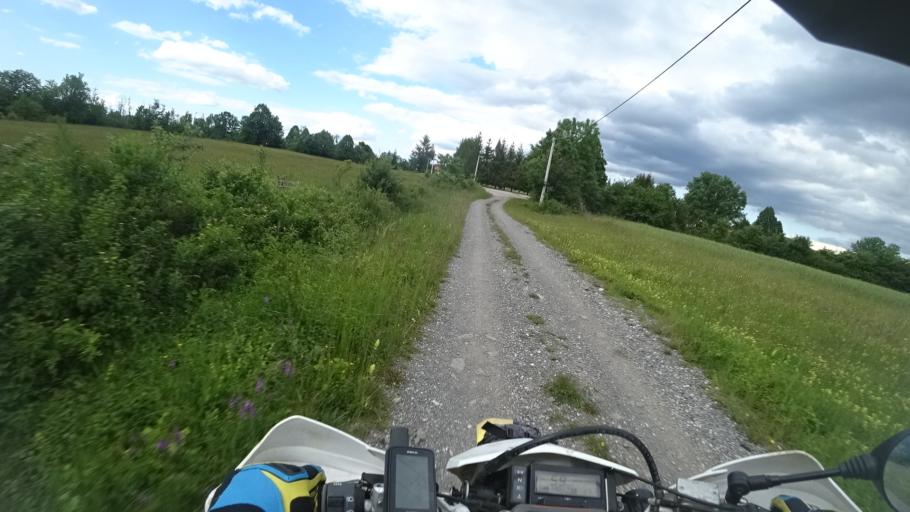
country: HR
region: Zadarska
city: Obrovac
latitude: 44.3566
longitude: 15.6578
